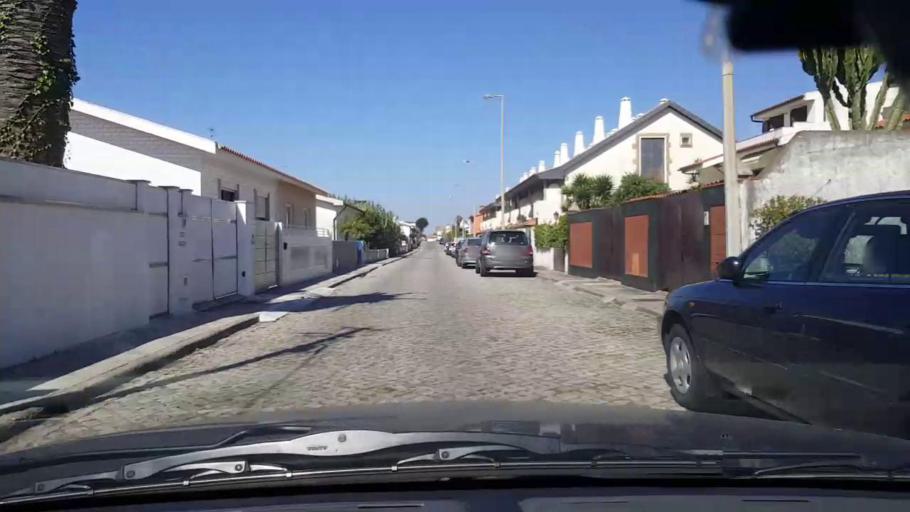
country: PT
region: Porto
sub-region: Vila do Conde
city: Arvore
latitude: 41.3063
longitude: -8.7355
